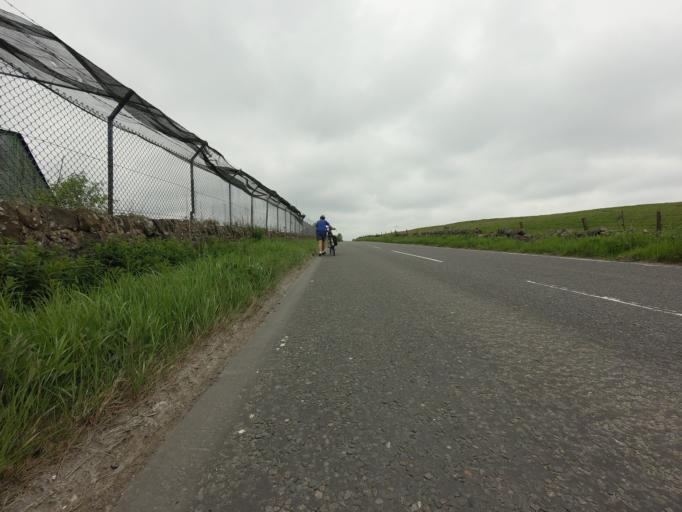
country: GB
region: Scotland
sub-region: Fife
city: Townhill
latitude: 56.1133
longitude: -3.4480
